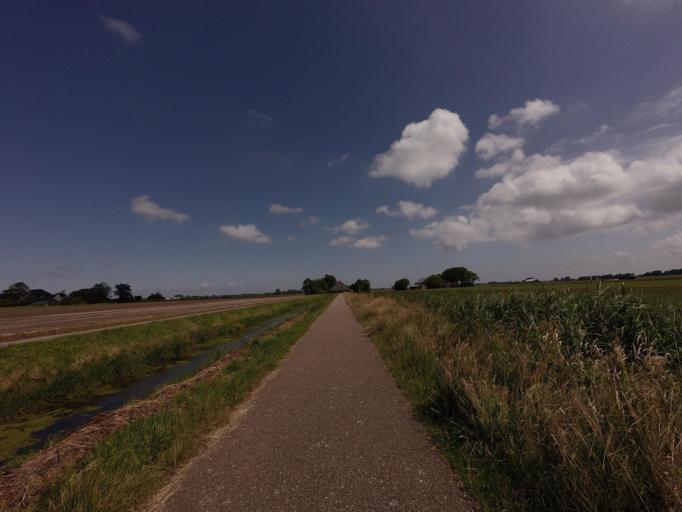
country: NL
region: North Holland
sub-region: Gemeente Schagen
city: Schagen
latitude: 52.8694
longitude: 4.8374
